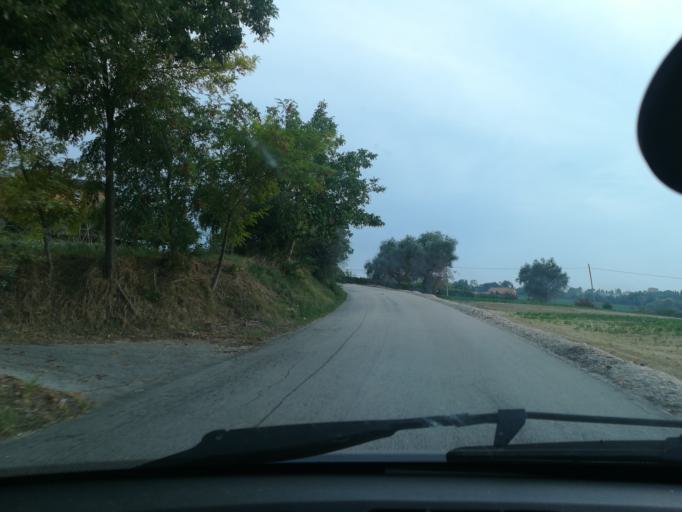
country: IT
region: The Marches
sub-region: Provincia di Macerata
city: Piediripa
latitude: 43.3010
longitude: 13.4798
